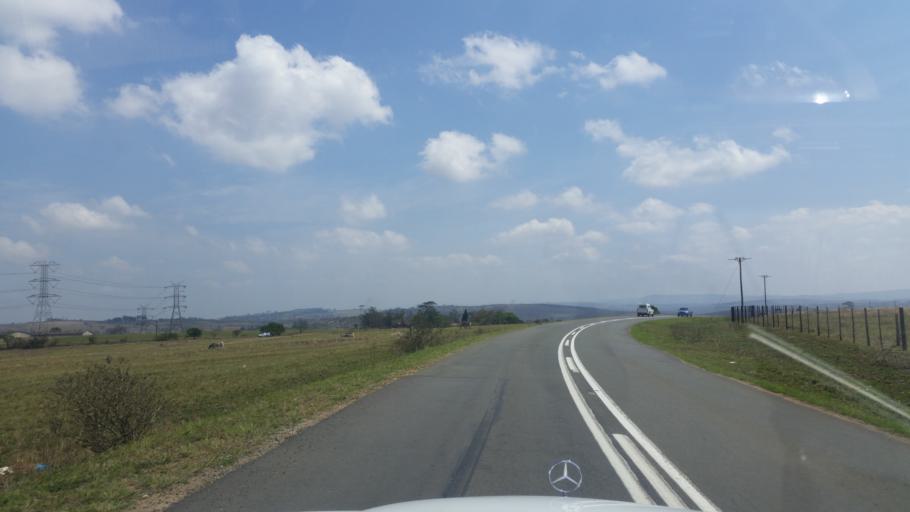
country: ZA
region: KwaZulu-Natal
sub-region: uMgungundlovu District Municipality
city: Camperdown
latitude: -29.6950
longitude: 30.4943
